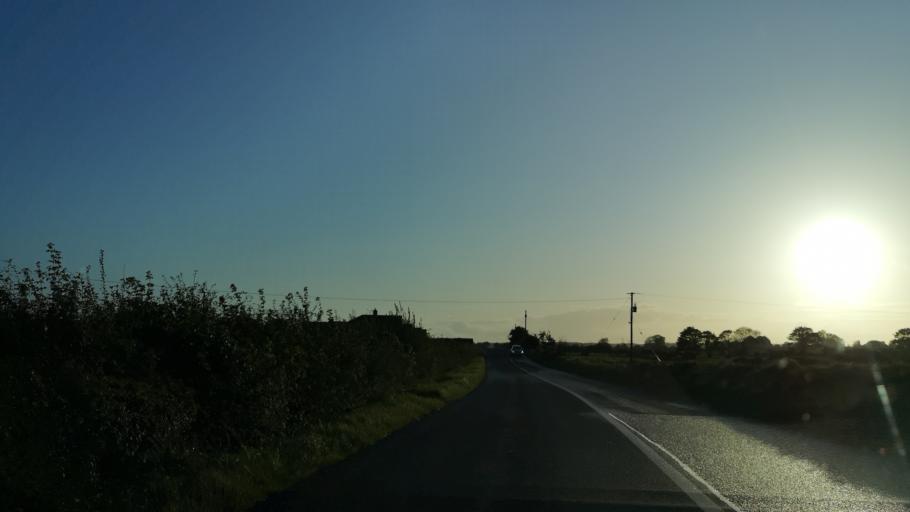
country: IE
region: Connaught
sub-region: Roscommon
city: Castlerea
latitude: 53.7552
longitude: -8.5216
